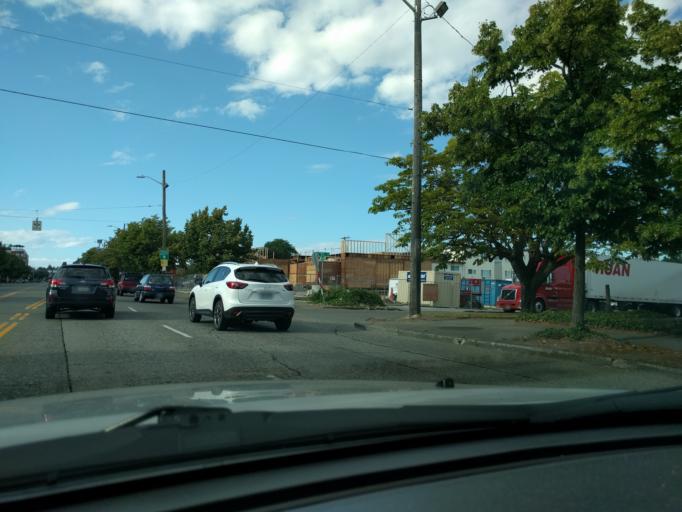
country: US
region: Washington
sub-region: King County
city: Seattle
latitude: 47.6655
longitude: -122.3762
